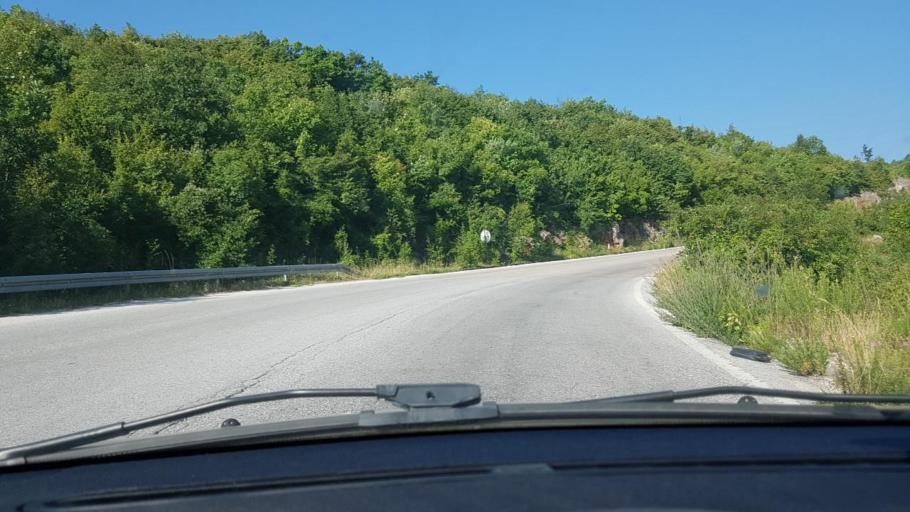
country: BA
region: Federation of Bosnia and Herzegovina
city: Rumboci
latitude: 43.8201
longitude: 17.4745
